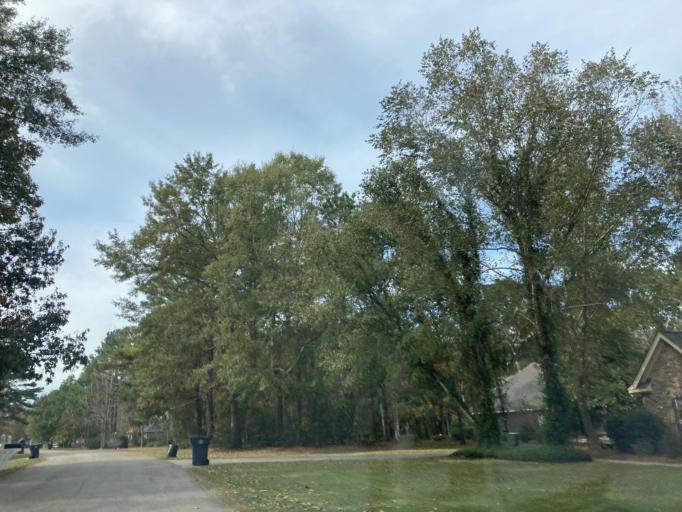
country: US
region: Mississippi
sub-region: Lamar County
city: West Hattiesburg
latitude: 31.3248
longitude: -89.4376
